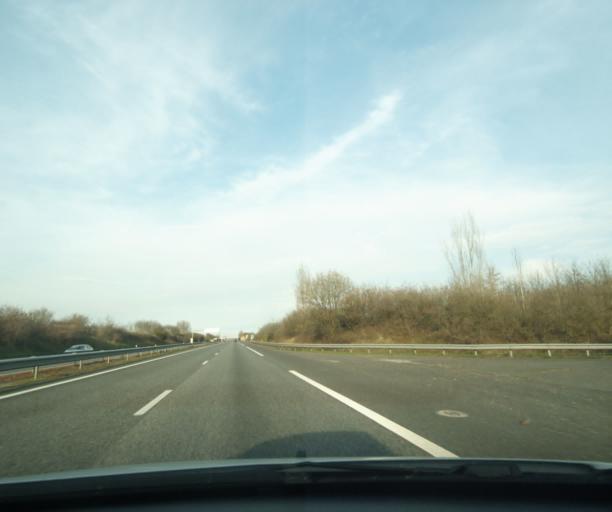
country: FR
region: Midi-Pyrenees
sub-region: Departement de la Haute-Garonne
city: Martres-Tolosane
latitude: 43.2002
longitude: 1.0036
